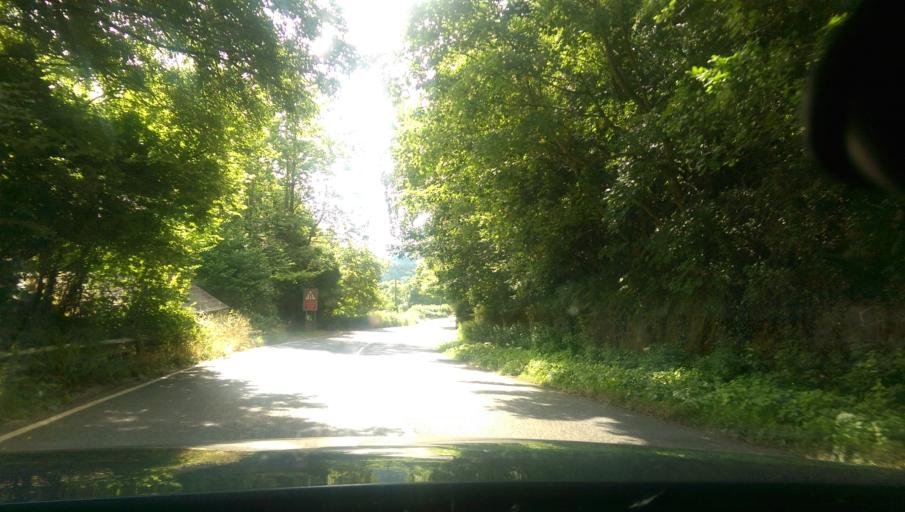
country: GB
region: England
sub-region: Devon
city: Okehampton
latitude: 50.7343
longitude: -3.9328
